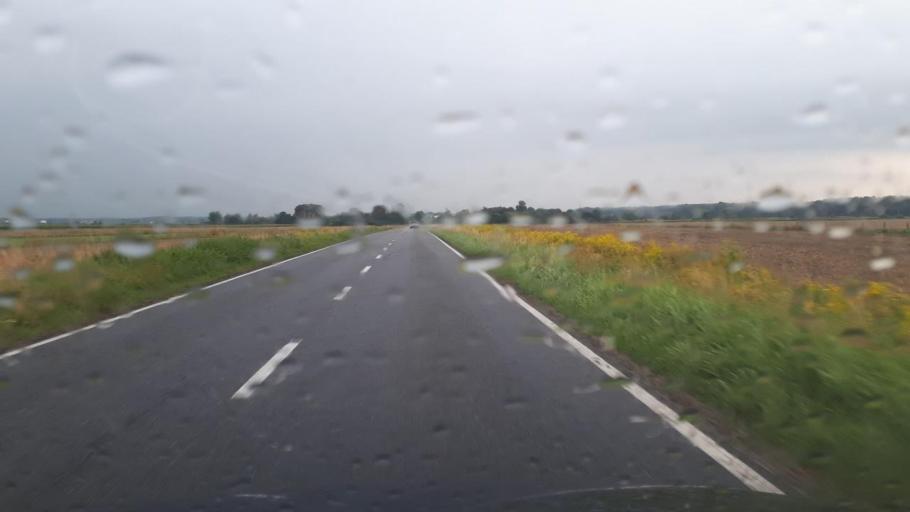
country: PL
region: Silesian Voivodeship
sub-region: Powiat tarnogorski
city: Wieszowa
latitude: 50.3622
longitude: 18.7181
